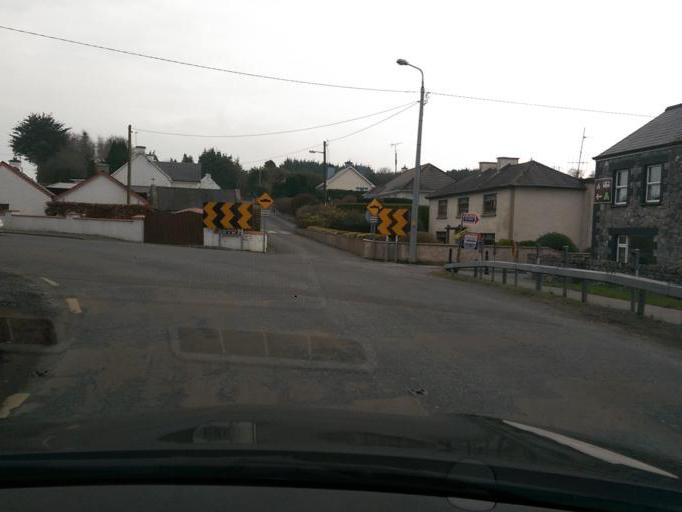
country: IE
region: Leinster
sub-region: An Iarmhi
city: Athlone
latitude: 53.4483
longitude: -7.8886
